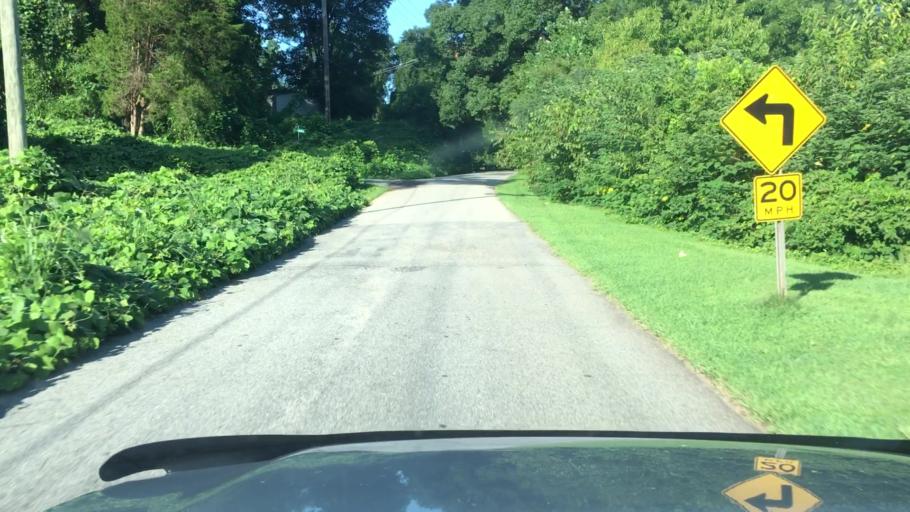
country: US
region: South Carolina
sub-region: Spartanburg County
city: Spartanburg
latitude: 34.9816
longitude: -81.9325
